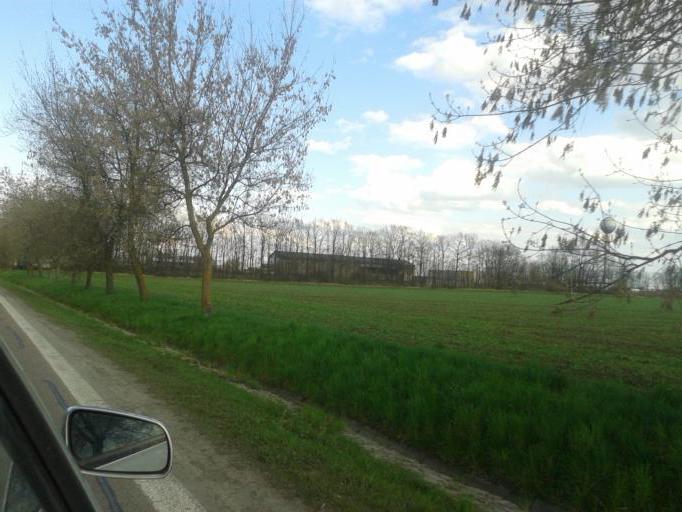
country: CZ
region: Central Bohemia
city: Rudna
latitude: 50.0410
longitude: 14.2506
